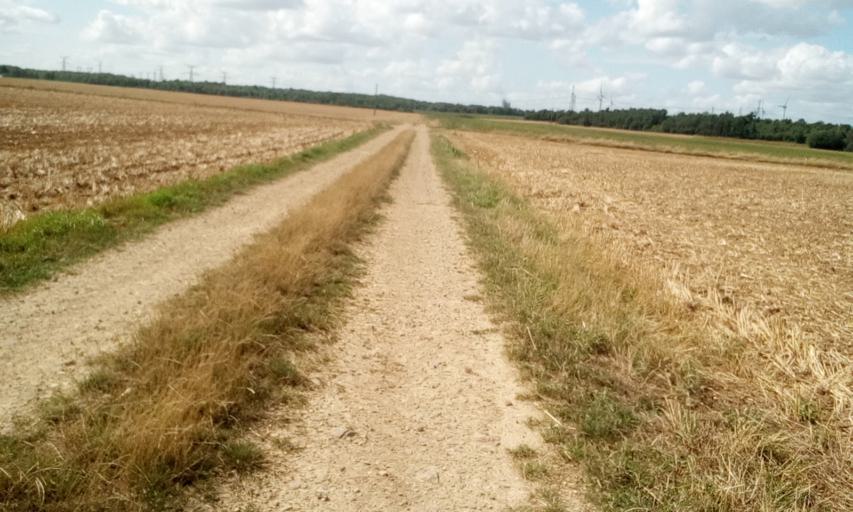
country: FR
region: Lower Normandy
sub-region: Departement du Calvados
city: Bellengreville
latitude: 49.1096
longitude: -0.2297
